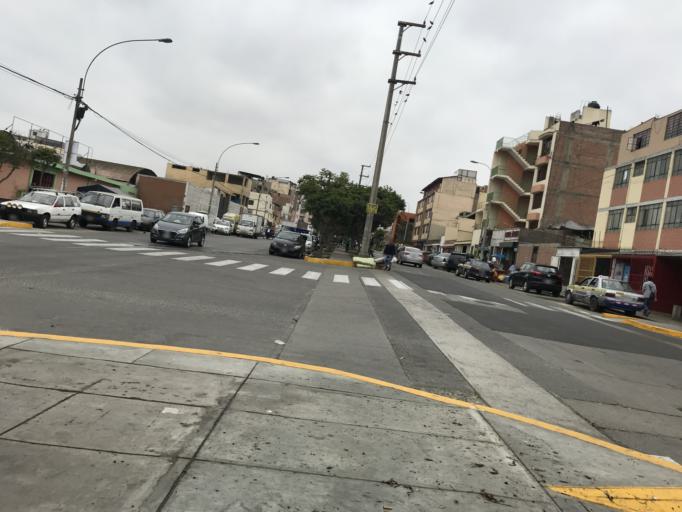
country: PE
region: Callao
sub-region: Callao
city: Callao
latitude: -12.0644
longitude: -77.0714
